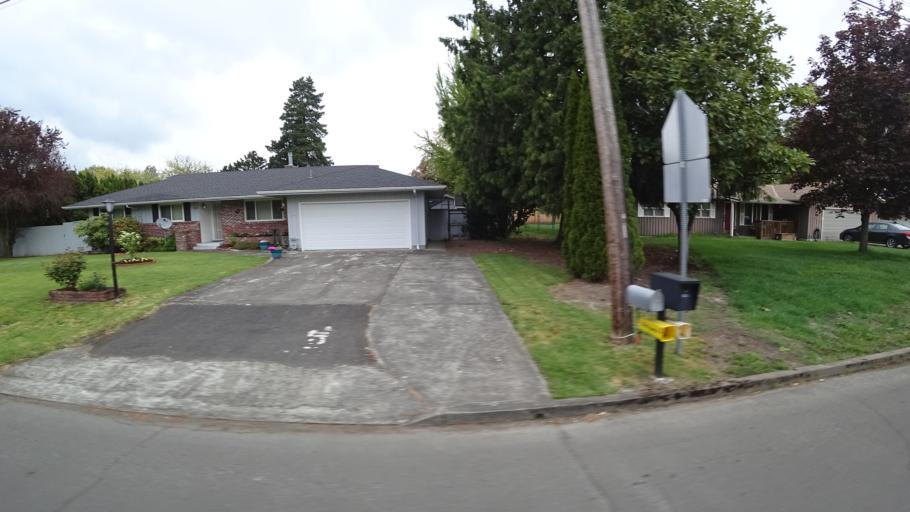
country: US
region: Oregon
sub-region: Washington County
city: Hillsboro
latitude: 45.5327
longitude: -122.9720
